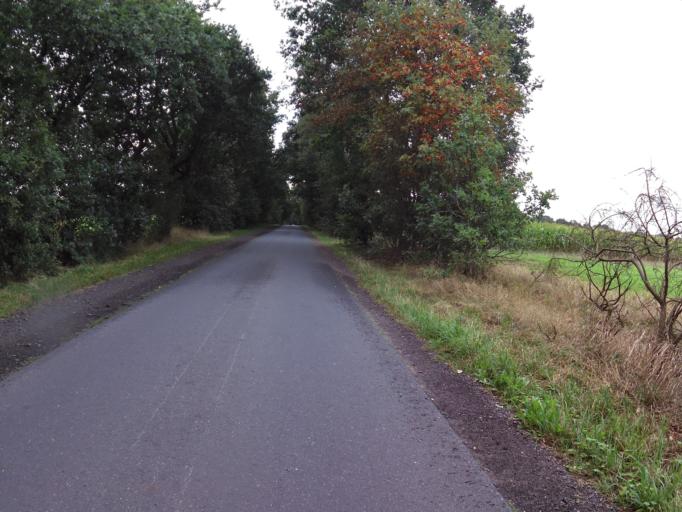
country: DE
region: Lower Saxony
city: Helvesiek
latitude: 53.2006
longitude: 9.4625
